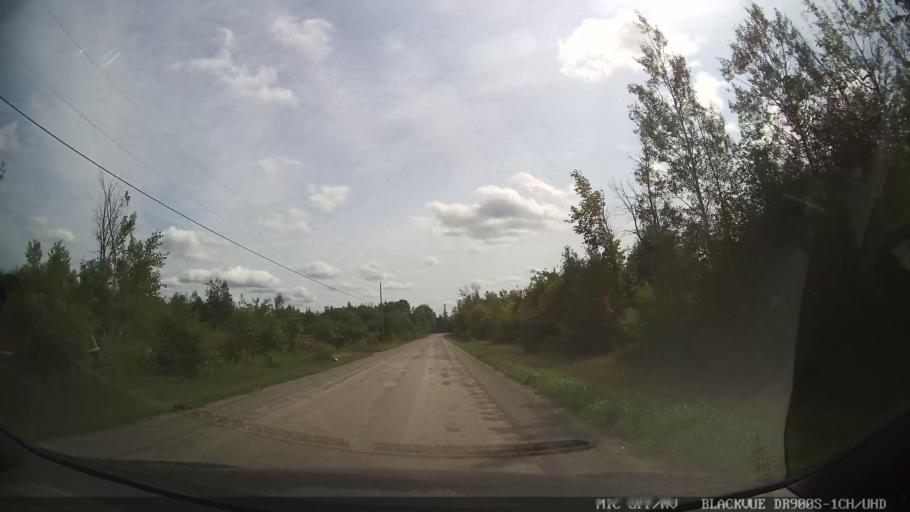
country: CA
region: Ontario
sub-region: Lanark County
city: Smiths Falls
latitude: 44.9831
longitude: -75.8829
